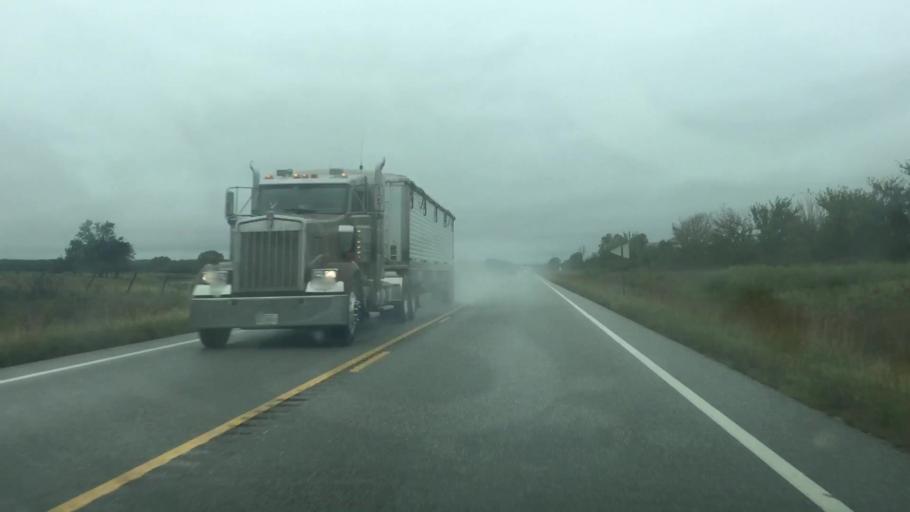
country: US
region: Kansas
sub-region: Anderson County
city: Garnett
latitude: 38.2946
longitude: -95.1982
